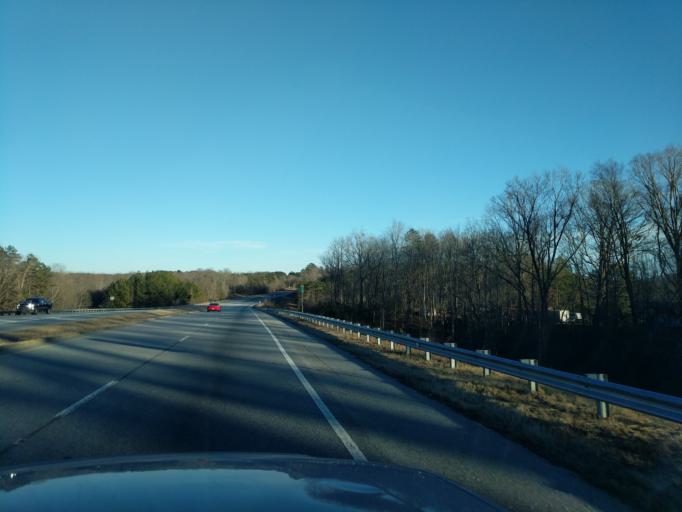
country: US
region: Georgia
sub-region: Stephens County
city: Toccoa
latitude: 34.5381
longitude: -83.3501
